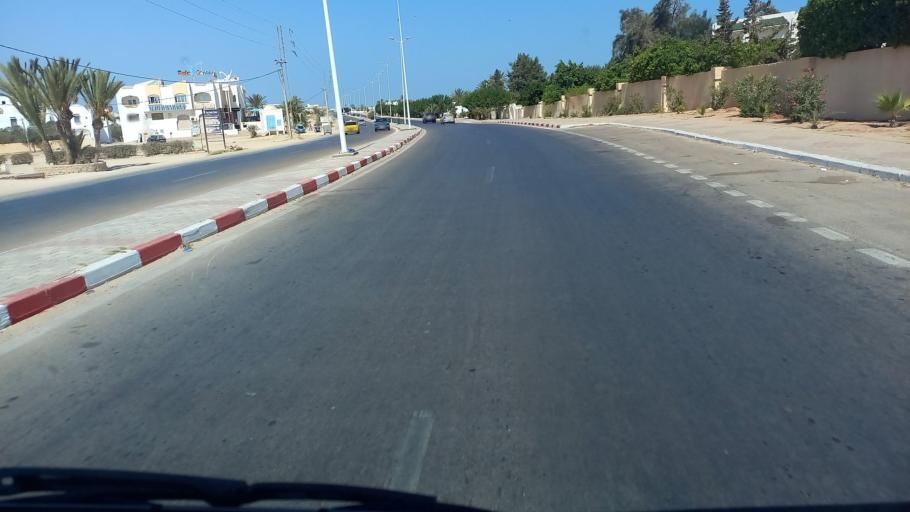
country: TN
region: Madanin
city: Midoun
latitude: 33.8593
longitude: 10.9738
